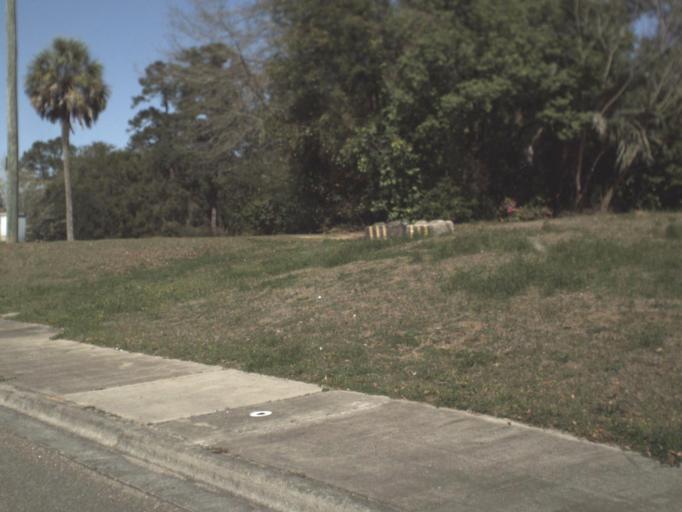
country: US
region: Florida
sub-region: Leon County
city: Tallahassee
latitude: 30.4489
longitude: -84.2264
